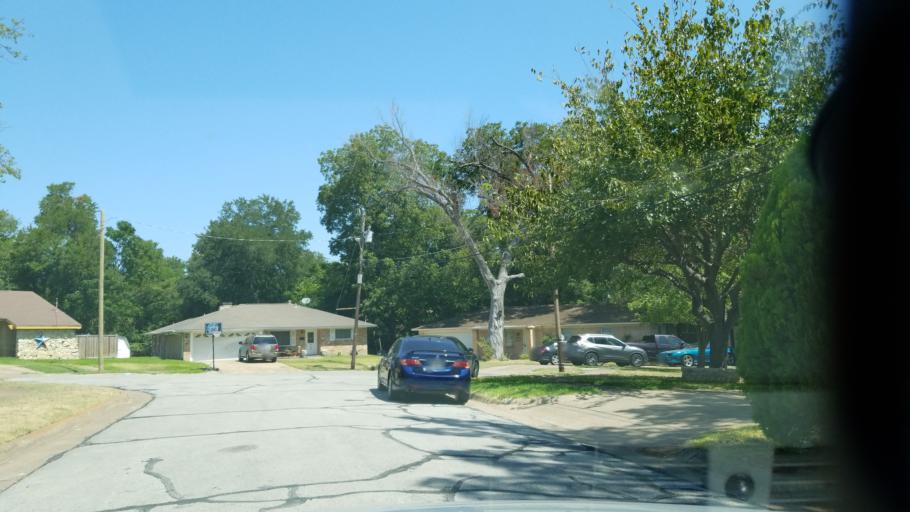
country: US
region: Texas
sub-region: Dallas County
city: Duncanville
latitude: 32.6527
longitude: -96.9013
